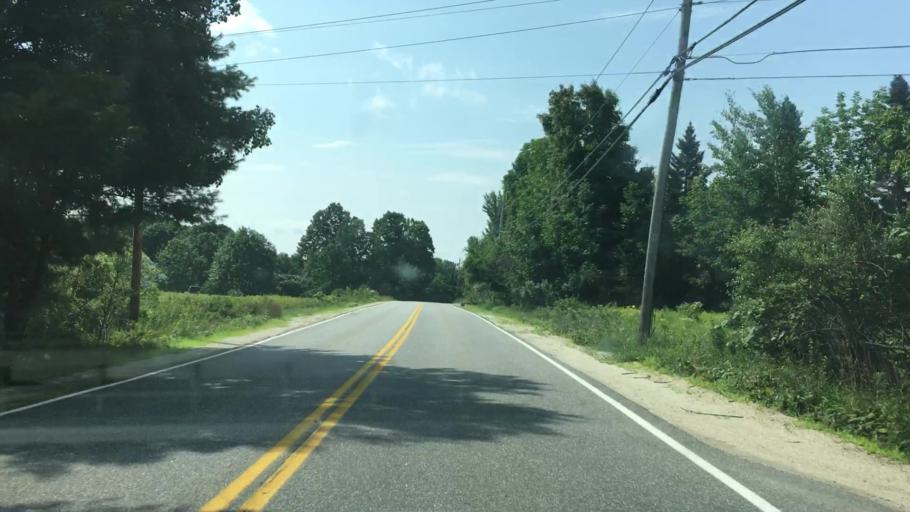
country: US
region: Maine
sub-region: Cumberland County
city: Raymond
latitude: 43.9426
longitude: -70.4385
